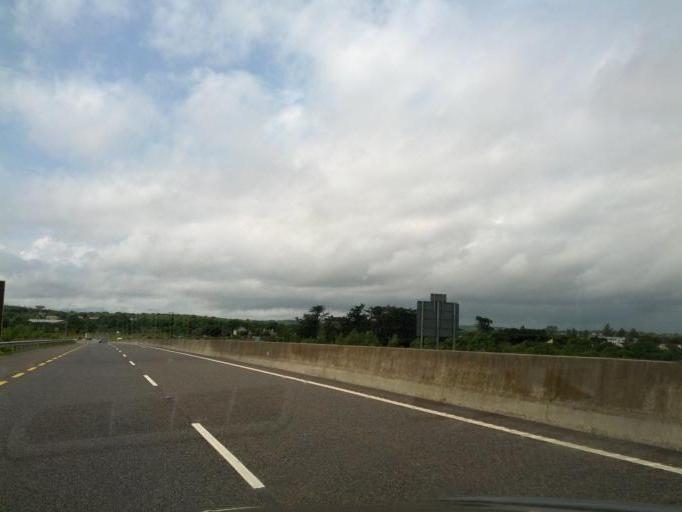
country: IE
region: Munster
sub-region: An Clar
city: Ennis
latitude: 52.8255
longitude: -8.9711
